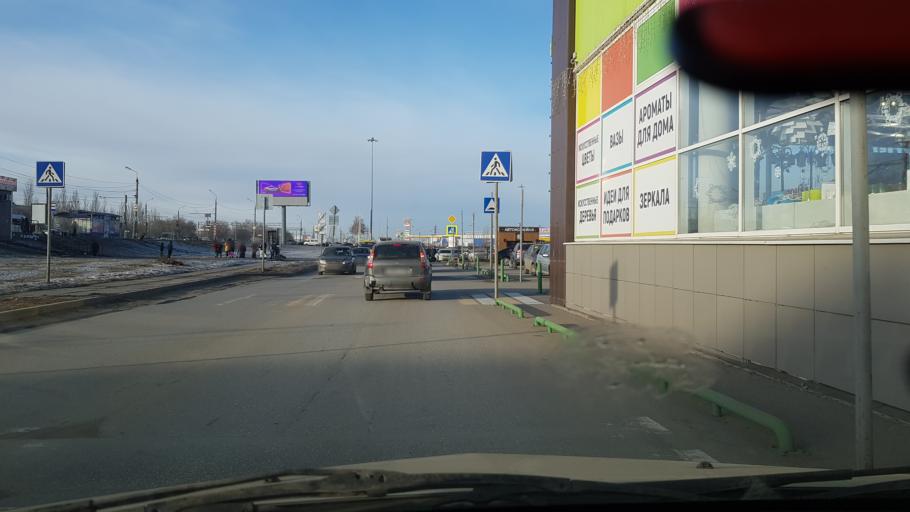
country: RU
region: Samara
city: Tol'yatti
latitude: 53.5394
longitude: 49.3900
